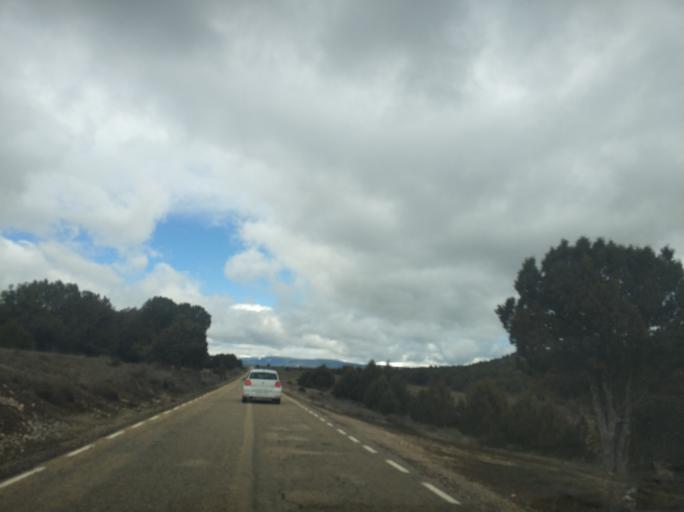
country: ES
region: Castille and Leon
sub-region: Provincia de Soria
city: Abejar
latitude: 41.7894
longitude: -2.7686
